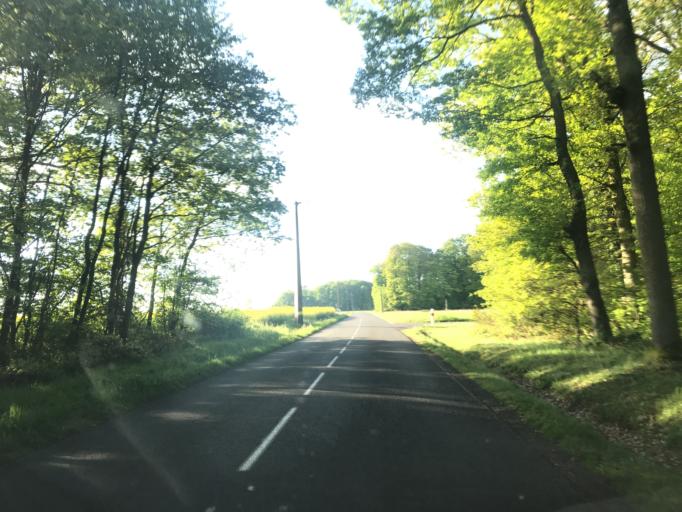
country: FR
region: Haute-Normandie
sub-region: Departement de l'Eure
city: Marcilly-sur-Eure
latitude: 48.8721
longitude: 1.3030
